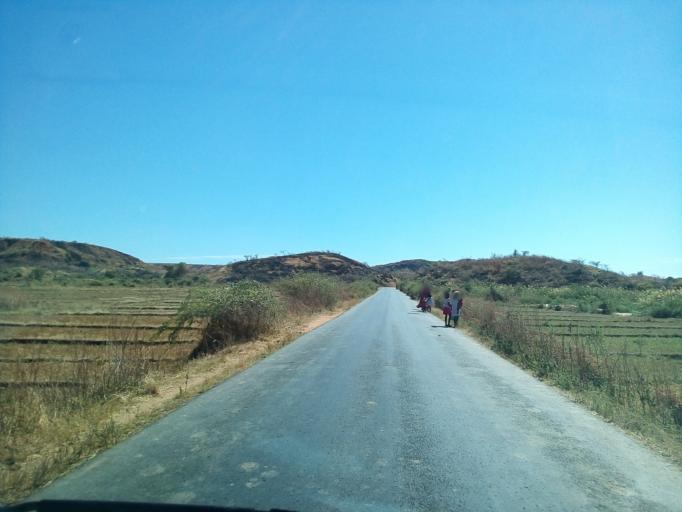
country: MG
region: Boeny
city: Ambato Boeny
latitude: -16.3757
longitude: 46.9640
